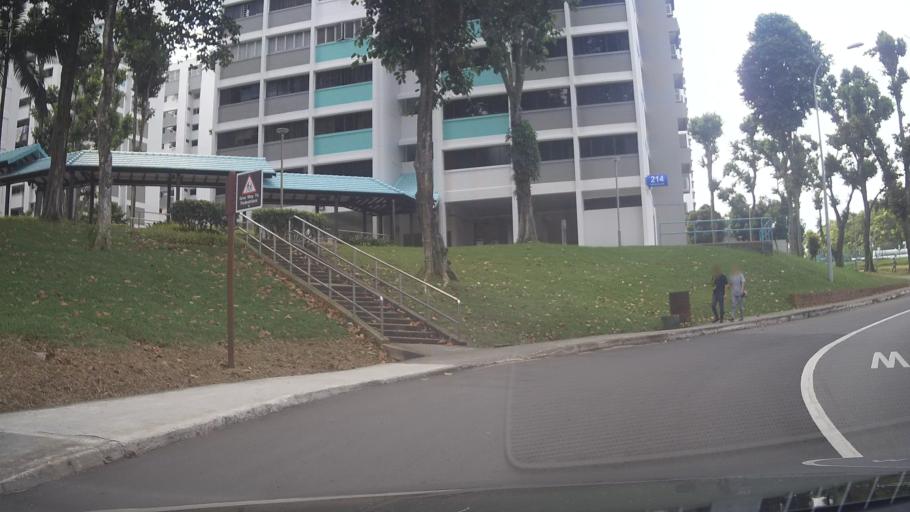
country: MY
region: Johor
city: Johor Bahru
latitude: 1.4472
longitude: 103.7716
